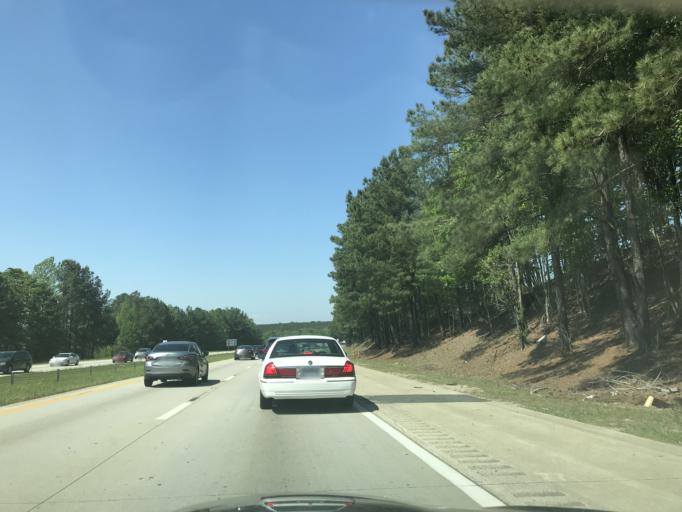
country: US
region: North Carolina
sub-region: Wake County
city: Garner
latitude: 35.6153
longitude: -78.5671
